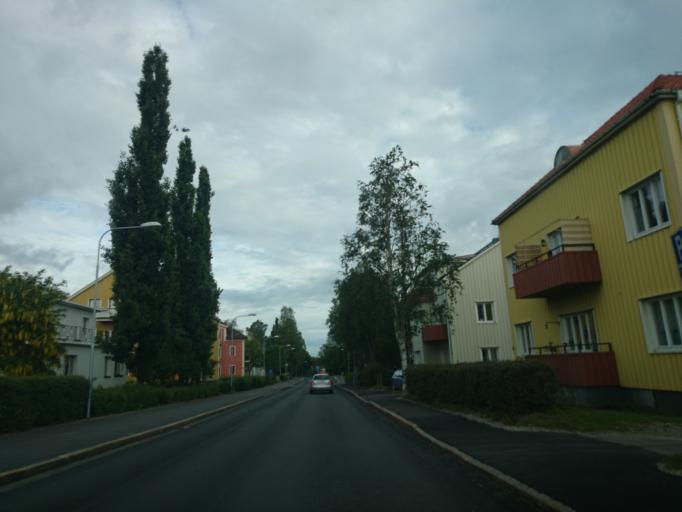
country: SE
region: Vaesternorrland
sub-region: Sundsvalls Kommun
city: Sundsvall
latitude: 62.3817
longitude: 17.3227
